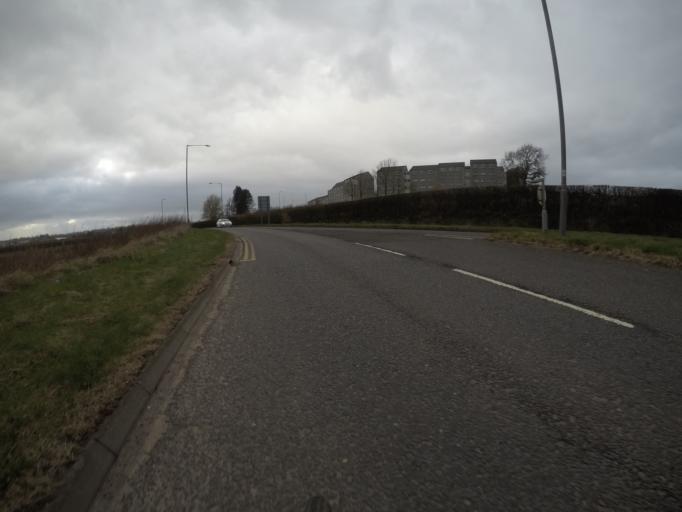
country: GB
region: Scotland
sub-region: East Ayrshire
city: Crosshouse
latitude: 55.6115
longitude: -4.5336
